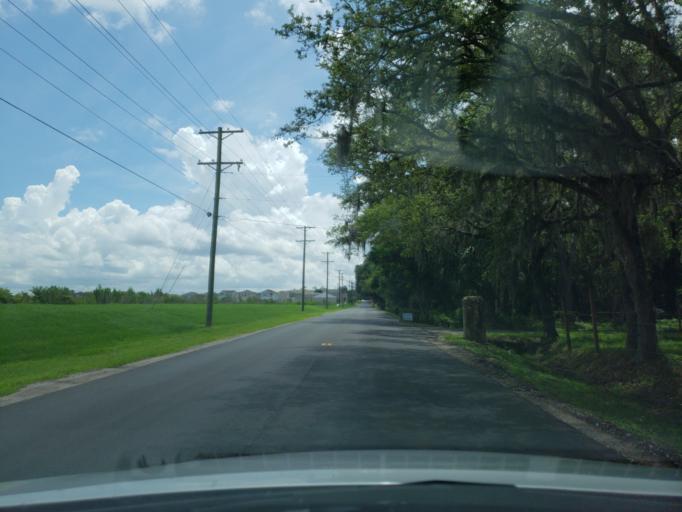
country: US
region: Florida
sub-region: Hillsborough County
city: Riverview
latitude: 27.8864
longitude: -82.3168
